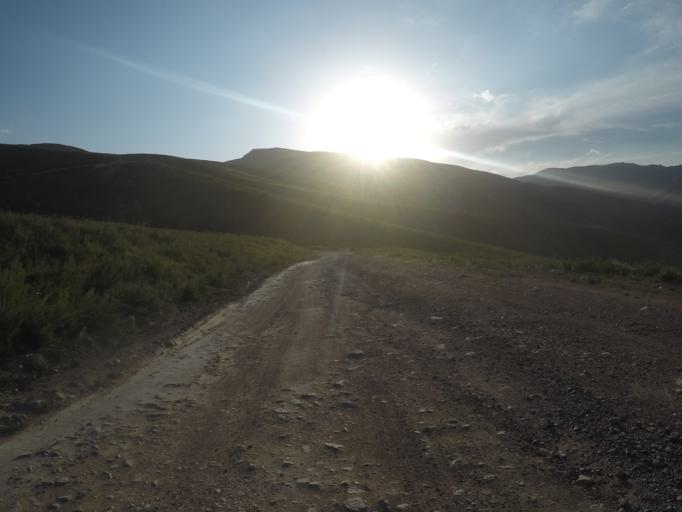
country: KG
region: Chuy
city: Bishkek
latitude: 42.6533
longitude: 74.6553
